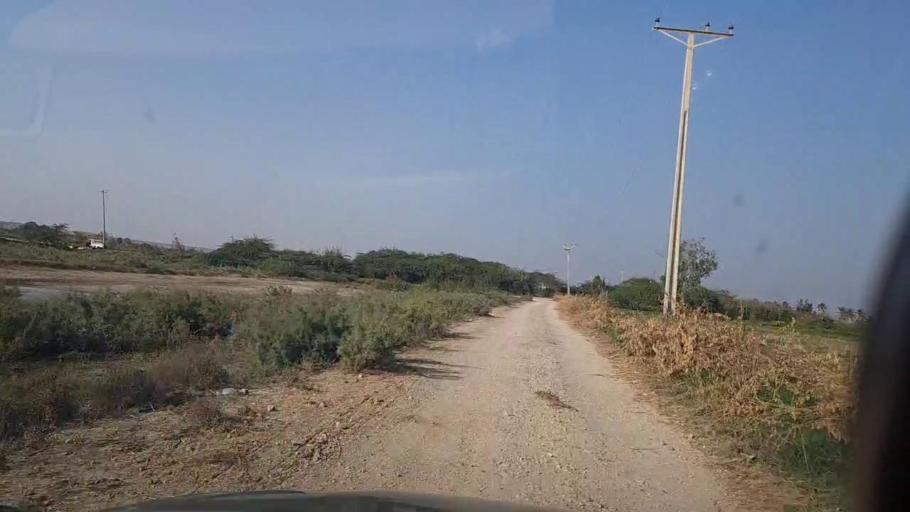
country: PK
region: Sindh
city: Thatta
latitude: 24.6070
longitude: 67.8746
